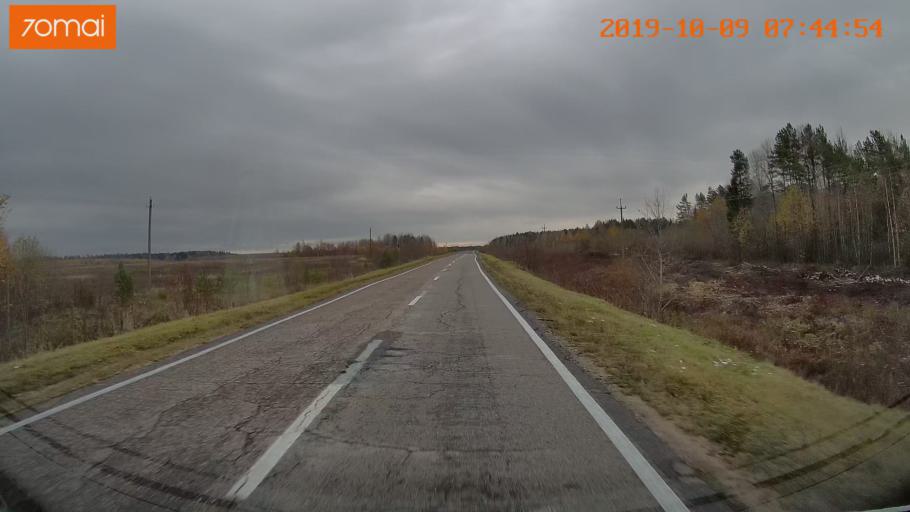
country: RU
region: Jaroslavl
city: Kukoboy
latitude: 58.6515
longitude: 39.7554
